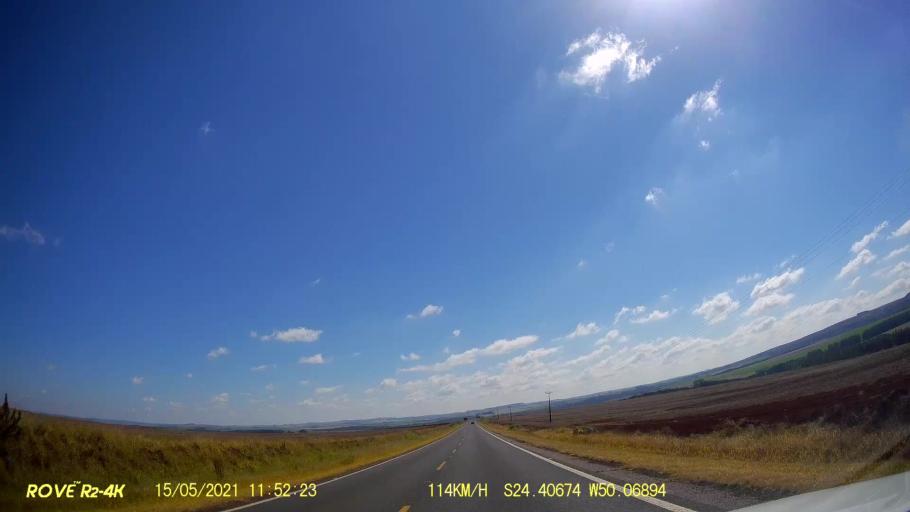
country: BR
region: Parana
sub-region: Pirai Do Sul
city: Pirai do Sul
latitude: -24.4066
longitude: -50.0688
